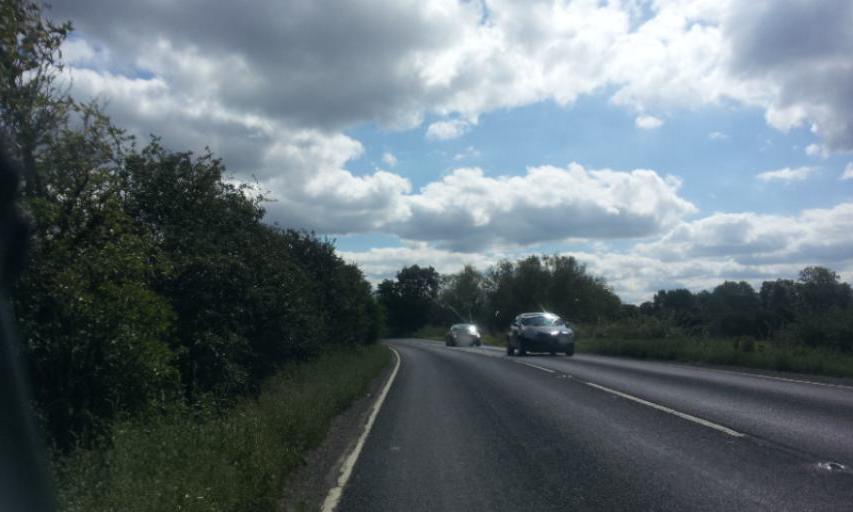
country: GB
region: England
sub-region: Kent
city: Marden
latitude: 51.2036
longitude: 0.5170
